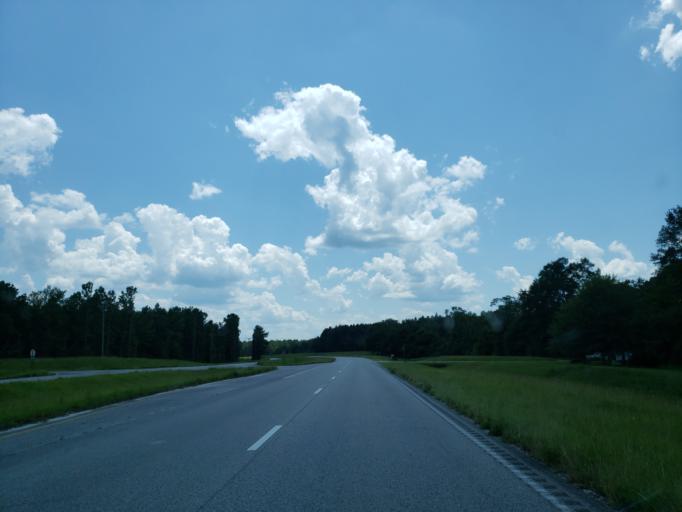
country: US
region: Mississippi
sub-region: Greene County
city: Leakesville
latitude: 31.3526
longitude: -88.5042
